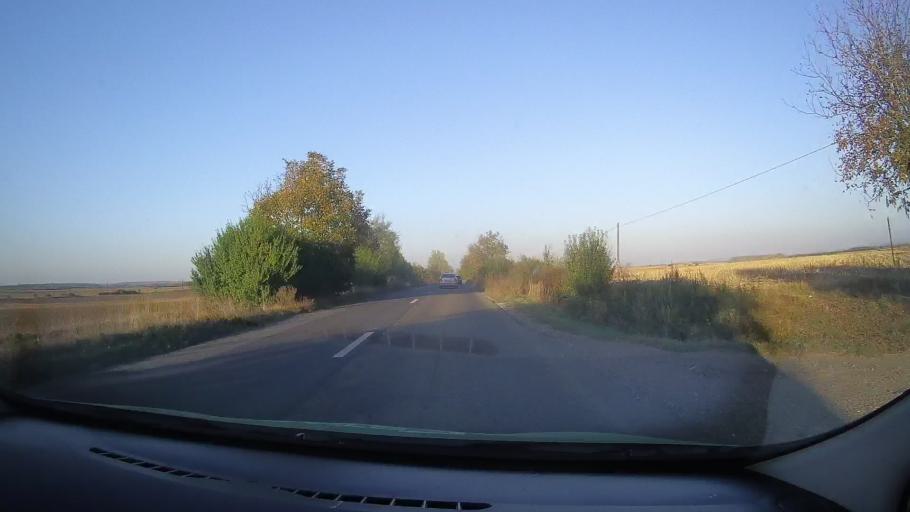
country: RO
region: Bihor
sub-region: Comuna Salard
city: Salard
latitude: 47.2024
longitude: 22.0106
